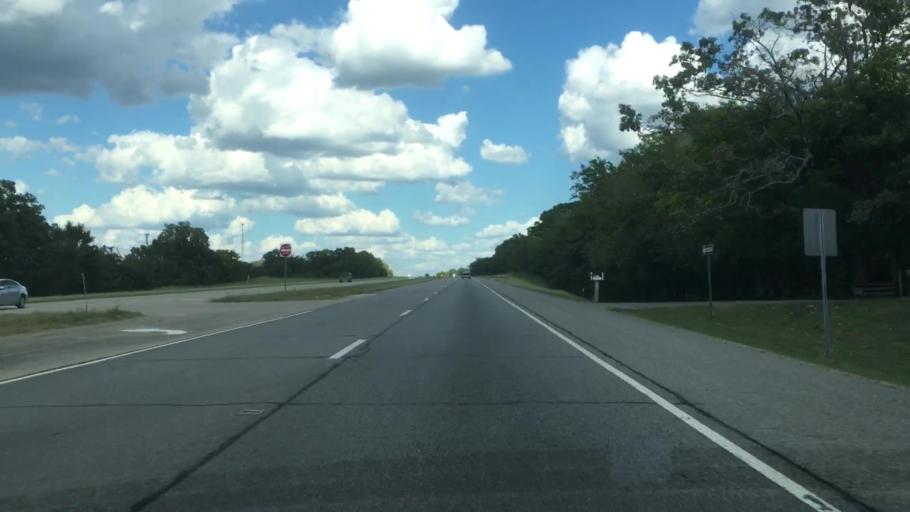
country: US
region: Oklahoma
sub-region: Cherokee County
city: Park Hill
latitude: 35.8045
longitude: -95.0820
